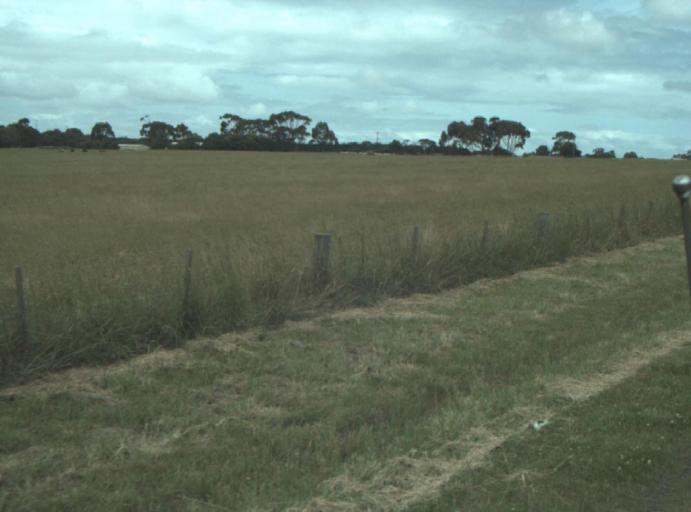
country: AU
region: Victoria
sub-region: Greater Geelong
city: Wandana Heights
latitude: -38.2264
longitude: 144.2990
